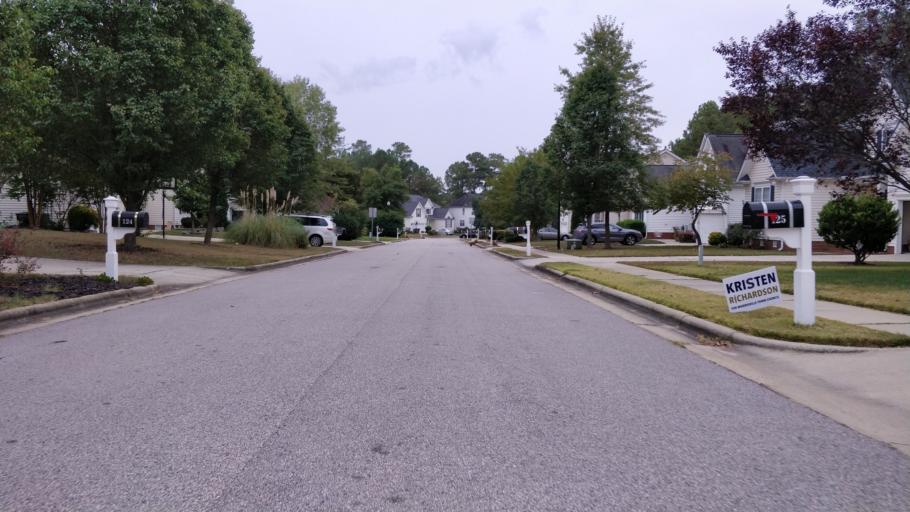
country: US
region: North Carolina
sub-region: Wake County
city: Morrisville
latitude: 35.8208
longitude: -78.8373
